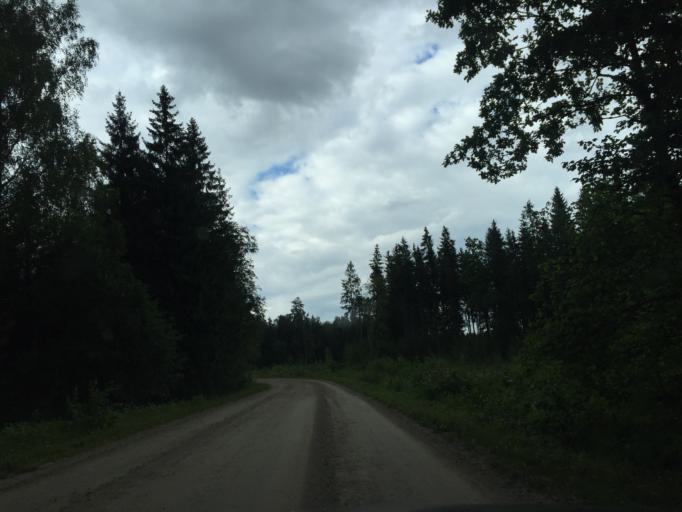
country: LV
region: Malpils
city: Malpils
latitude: 56.9435
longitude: 25.0033
